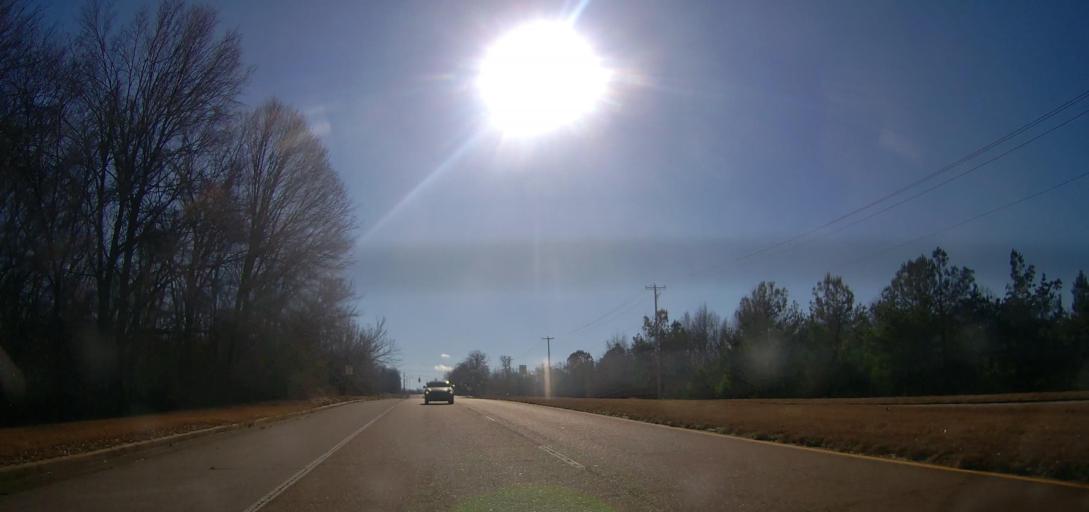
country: US
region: Tennessee
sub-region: Shelby County
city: Bartlett
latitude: 35.2446
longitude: -89.8969
